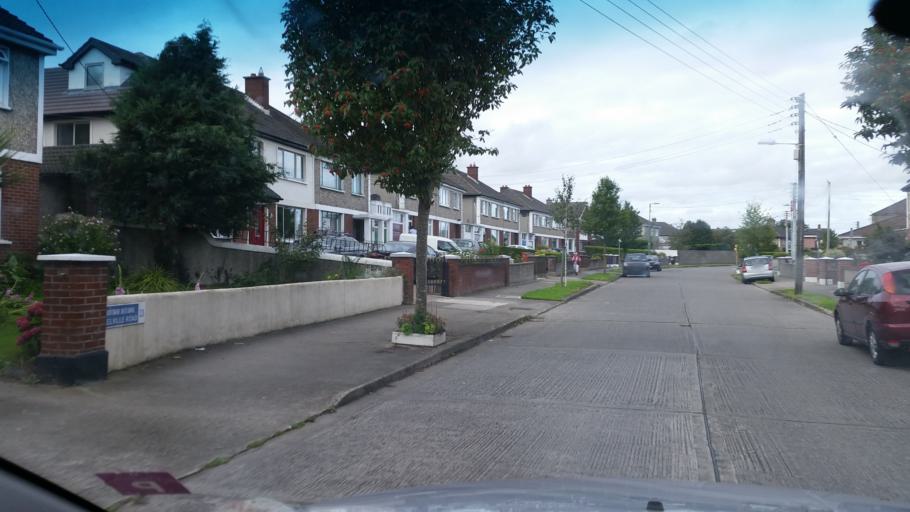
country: IE
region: Leinster
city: Glasnevin
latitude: 53.3877
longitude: -6.2721
